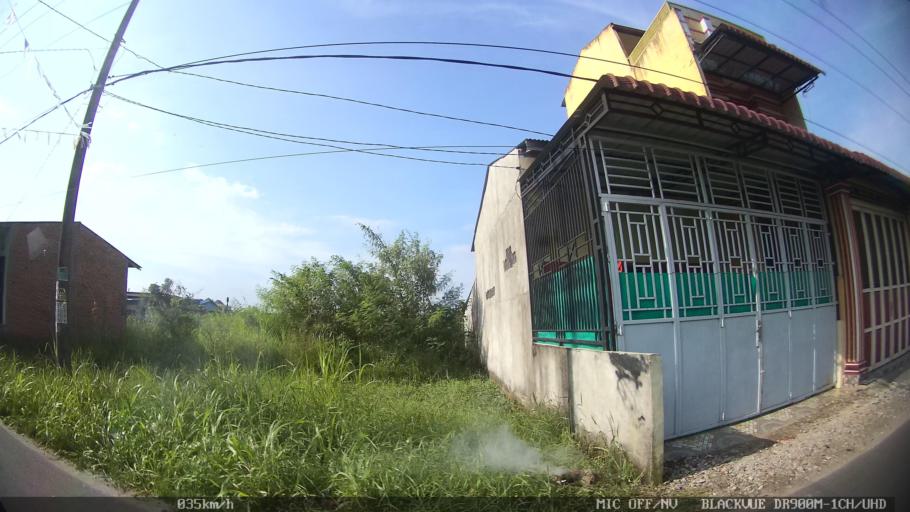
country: ID
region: North Sumatra
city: Medan
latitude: 3.5942
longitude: 98.7620
